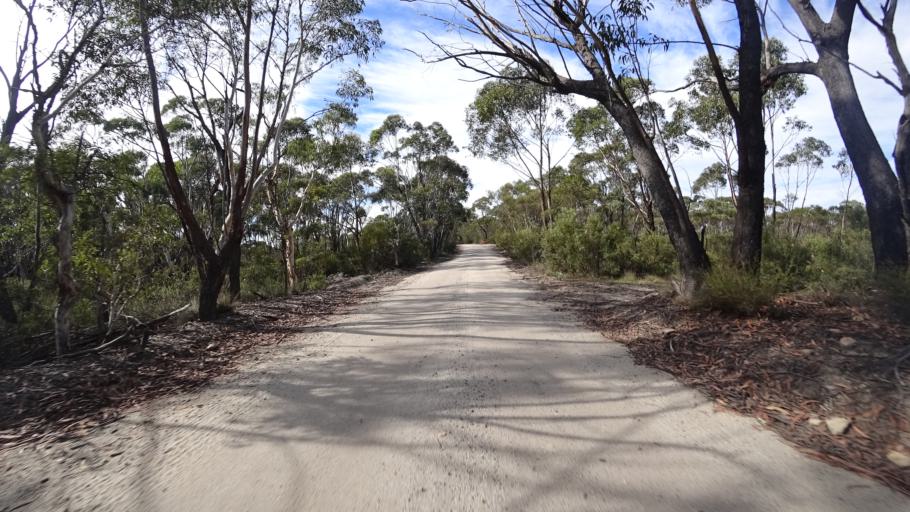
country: AU
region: New South Wales
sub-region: Lithgow
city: Lithgow
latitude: -33.5025
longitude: 150.1631
